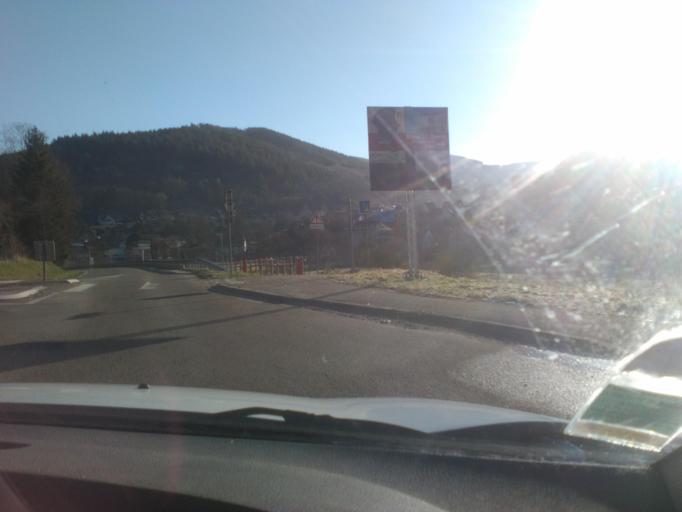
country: FR
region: Alsace
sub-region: Departement du Bas-Rhin
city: Rothau
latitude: 48.4177
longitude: 7.1834
